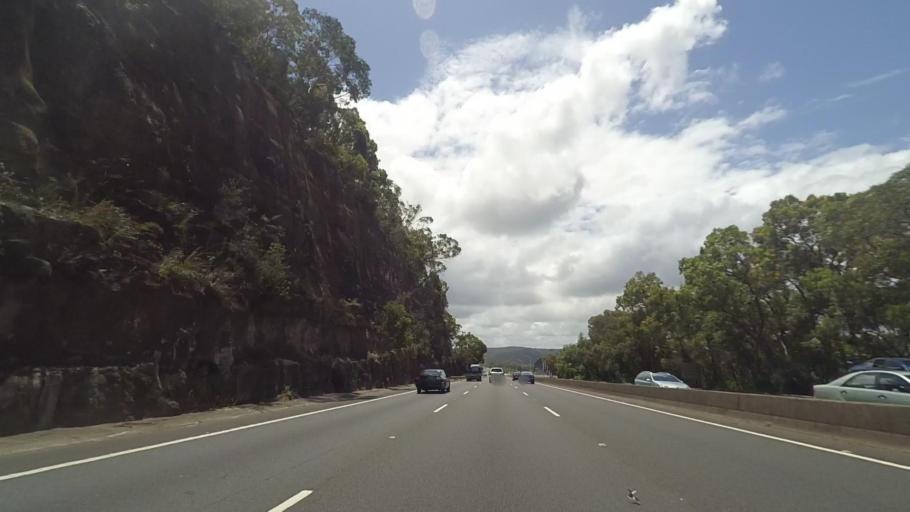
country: AU
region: New South Wales
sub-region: Hornsby Shire
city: Berowra
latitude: -33.5426
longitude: 151.1977
